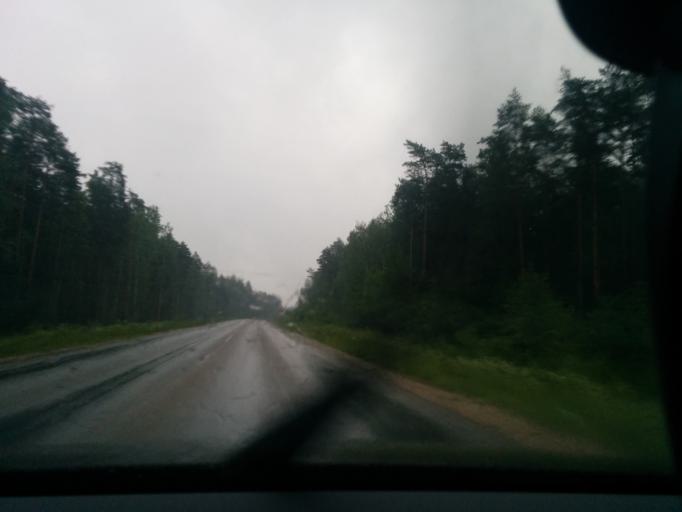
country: LV
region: Stopini
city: Ulbroka
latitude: 56.9151
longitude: 24.3212
